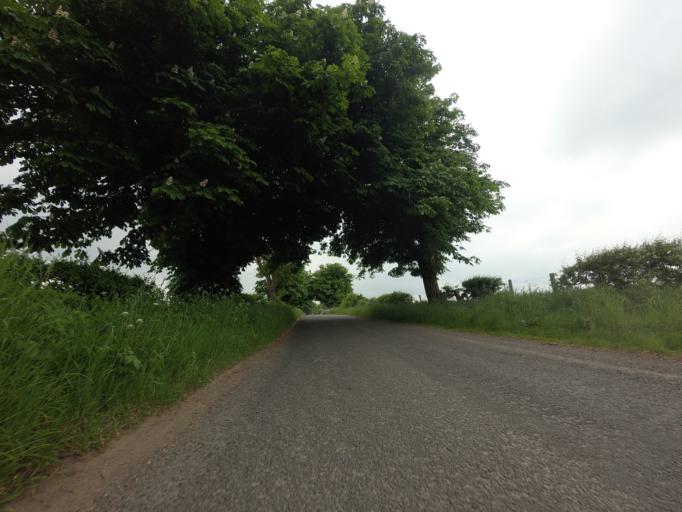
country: GB
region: Scotland
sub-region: Perth and Kinross
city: Kinross
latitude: 56.1867
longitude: -3.4345
